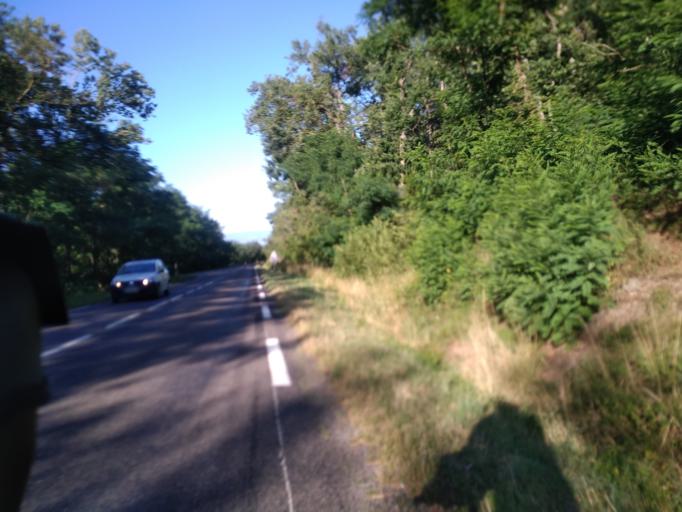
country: FR
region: Rhone-Alpes
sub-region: Departement de la Loire
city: Civens
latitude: 45.7398
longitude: 4.2968
